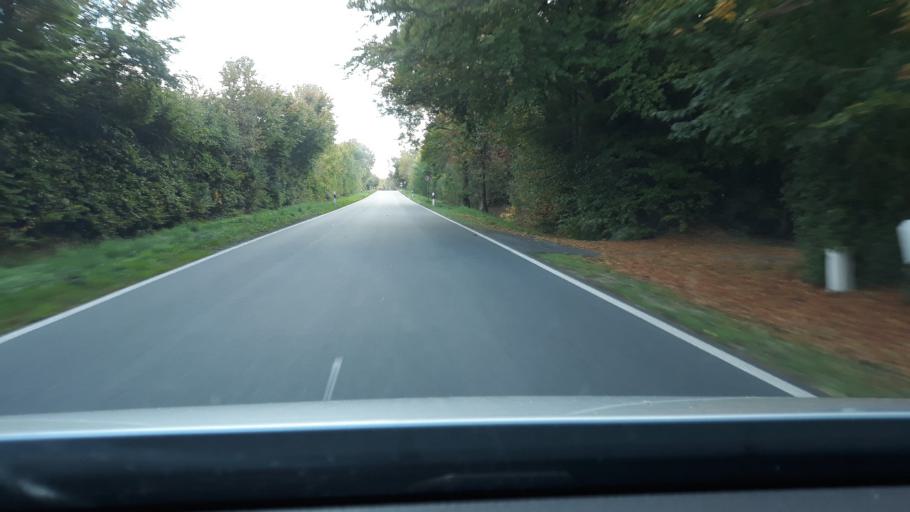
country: DE
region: Schleswig-Holstein
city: Idstedt
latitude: 54.5803
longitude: 9.4948
